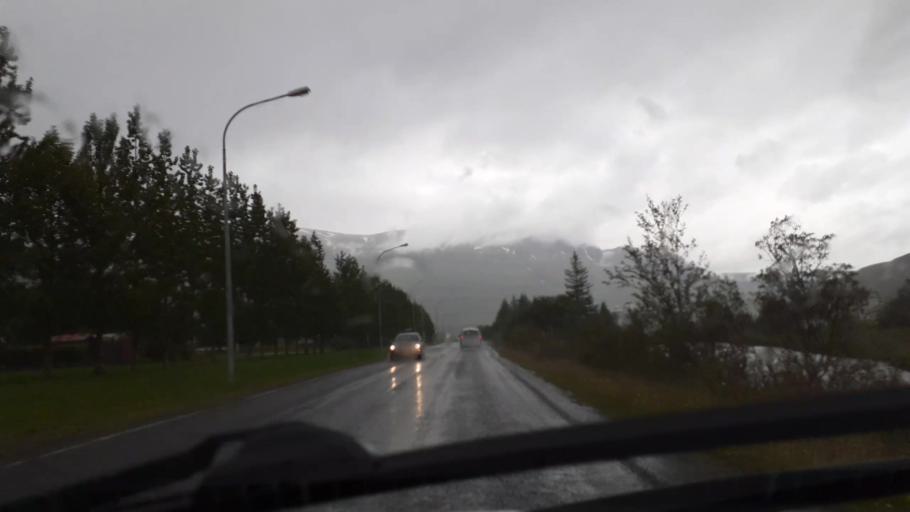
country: IS
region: East
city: Eskifjoerdur
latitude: 65.2573
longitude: -14.0122
